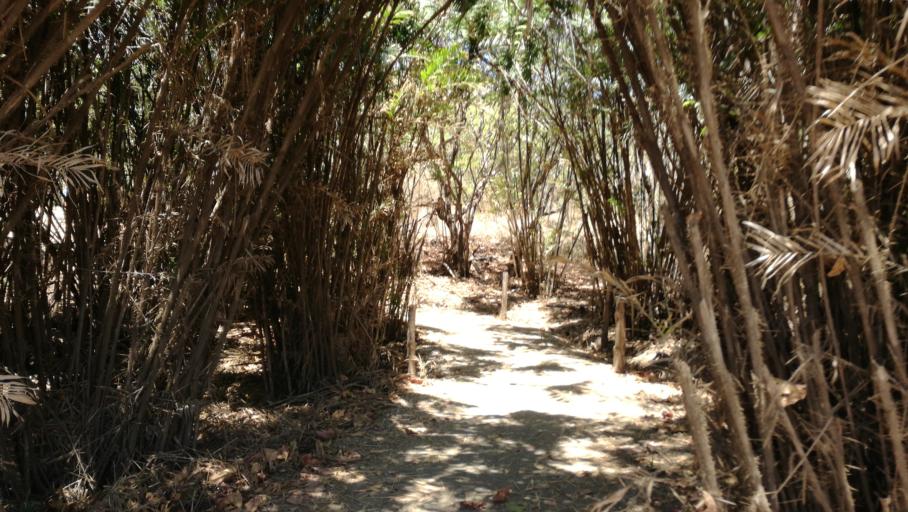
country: CR
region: Guanacaste
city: Samara
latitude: 9.8624
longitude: -85.4443
